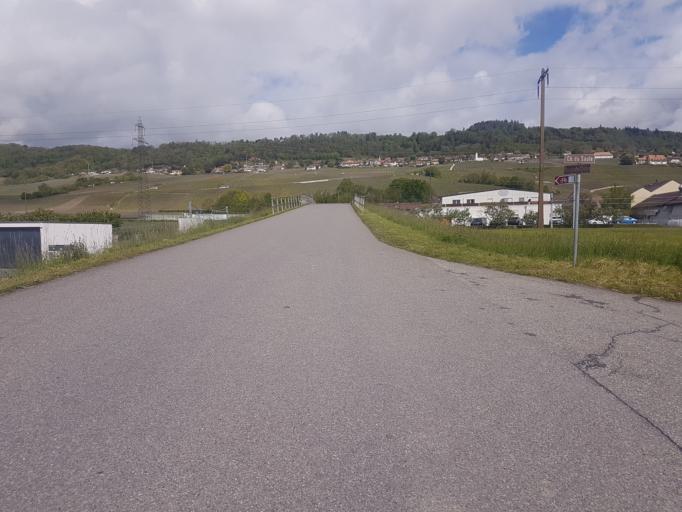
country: CH
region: Vaud
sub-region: Nyon District
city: Perroy
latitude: 46.4700
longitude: 6.3596
